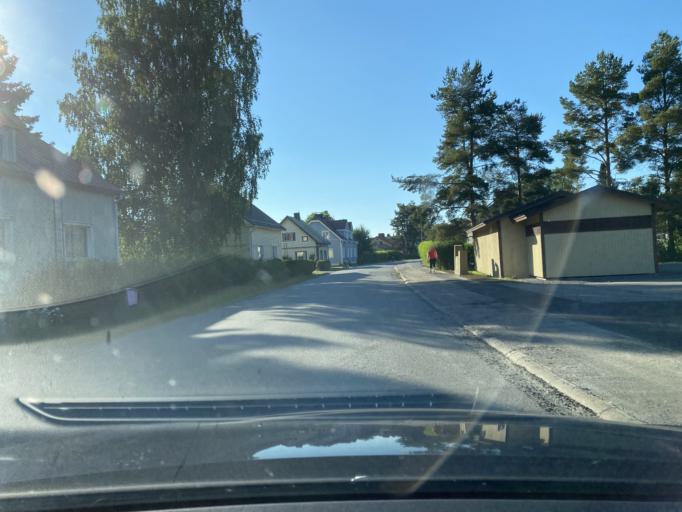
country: FI
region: Satakunta
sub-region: Pori
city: Huittinen
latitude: 61.1717
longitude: 22.6972
